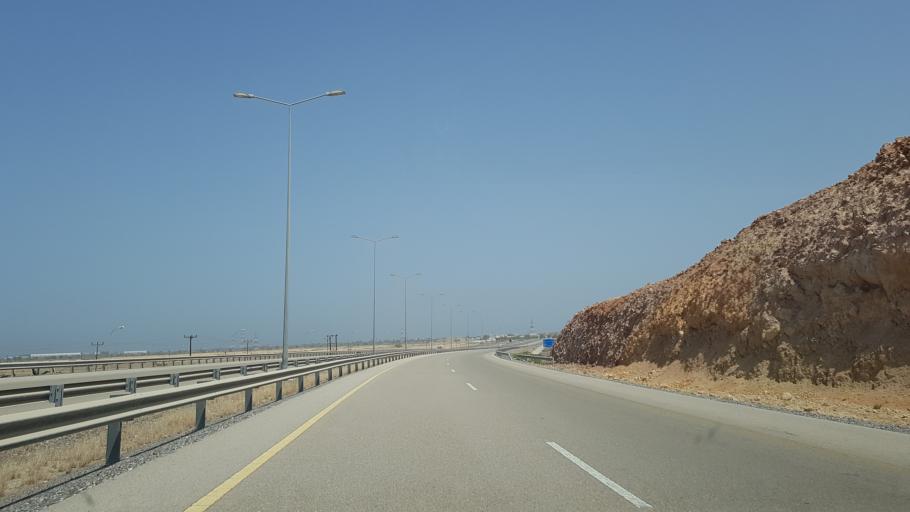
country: OM
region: Muhafazat Masqat
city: Muscat
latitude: 23.2134
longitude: 58.9353
